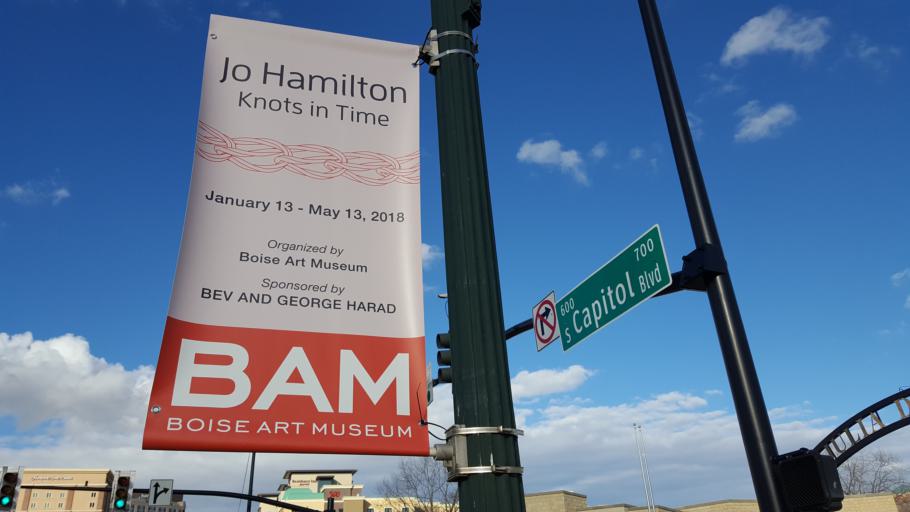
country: US
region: Idaho
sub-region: Ada County
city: Boise
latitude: 43.6106
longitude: -116.2075
